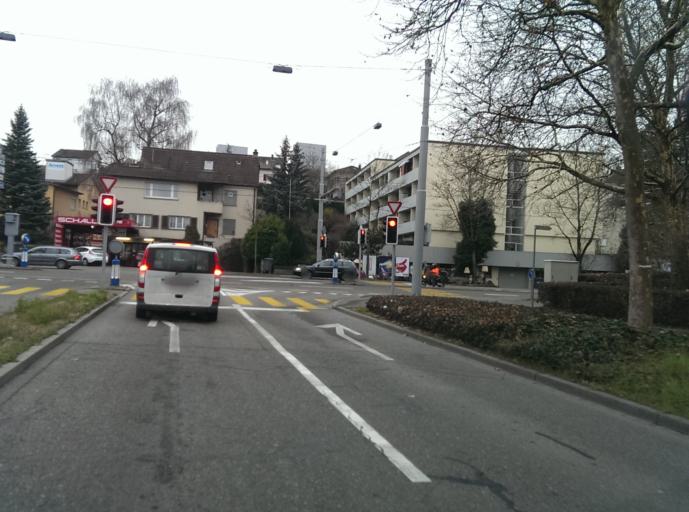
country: CH
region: Zurich
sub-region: Bezirk Zuerich
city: Zuerich (Kreis 9) / Altstetten
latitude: 47.3941
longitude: 8.4728
